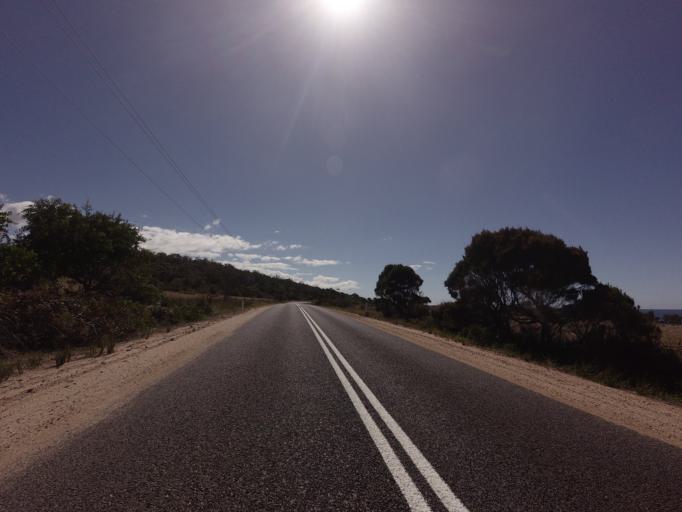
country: AU
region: Tasmania
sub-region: Break O'Day
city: St Helens
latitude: -41.7989
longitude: 148.2612
